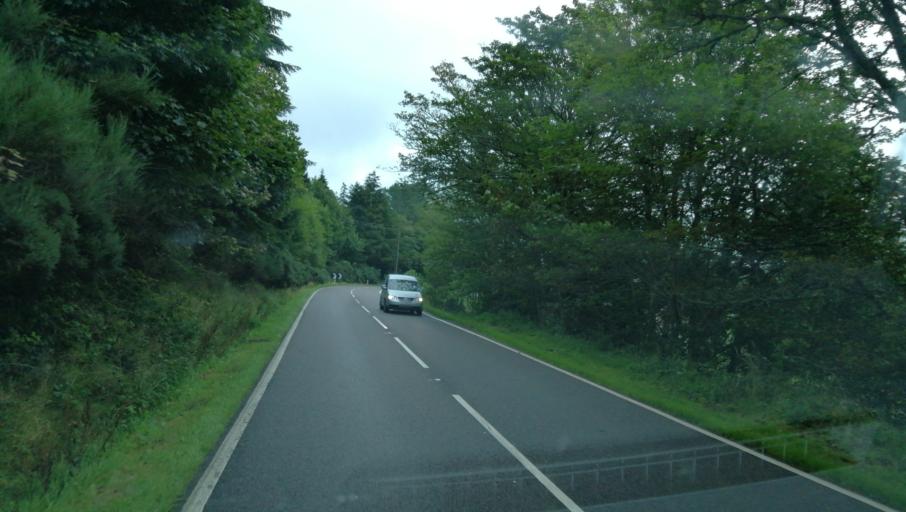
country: GB
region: Scotland
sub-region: Highland
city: Inverness
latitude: 57.4126
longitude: -4.3352
